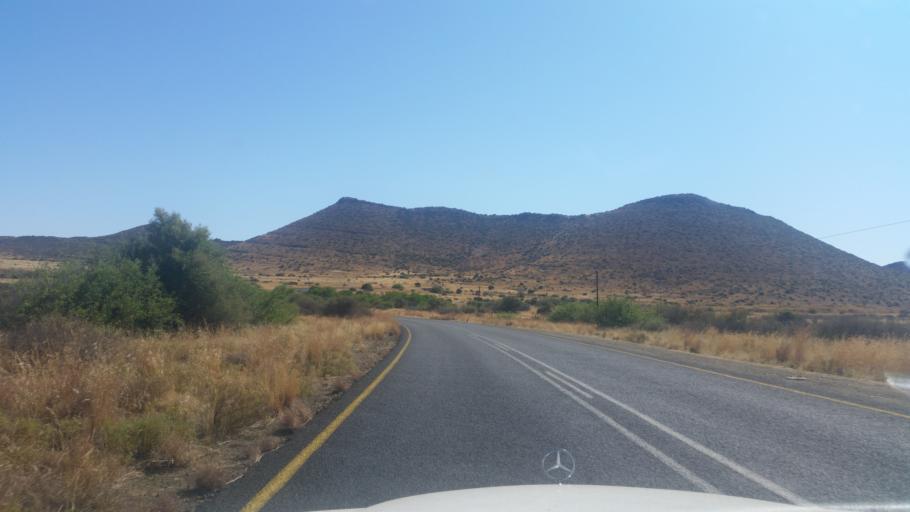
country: ZA
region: Orange Free State
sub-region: Xhariep District Municipality
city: Trompsburg
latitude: -30.4815
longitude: 25.9992
